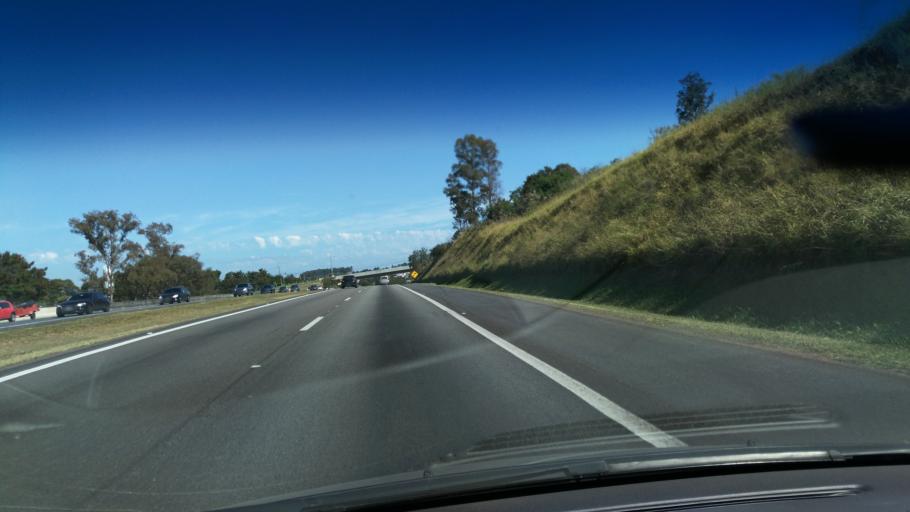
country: BR
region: Sao Paulo
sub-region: Valinhos
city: Valinhos
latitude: -22.9473
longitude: -47.0159
